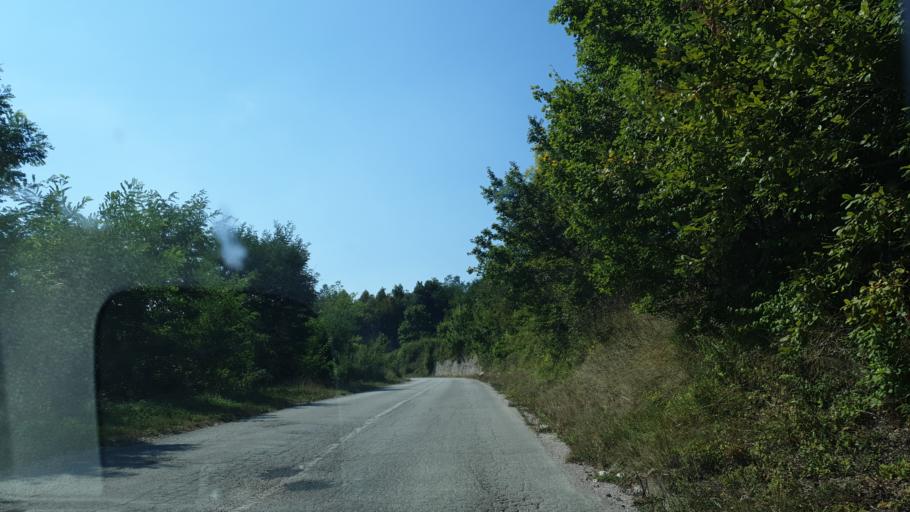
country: RS
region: Central Serbia
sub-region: Zlatiborski Okrug
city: Cajetina
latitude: 43.7141
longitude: 19.8299
